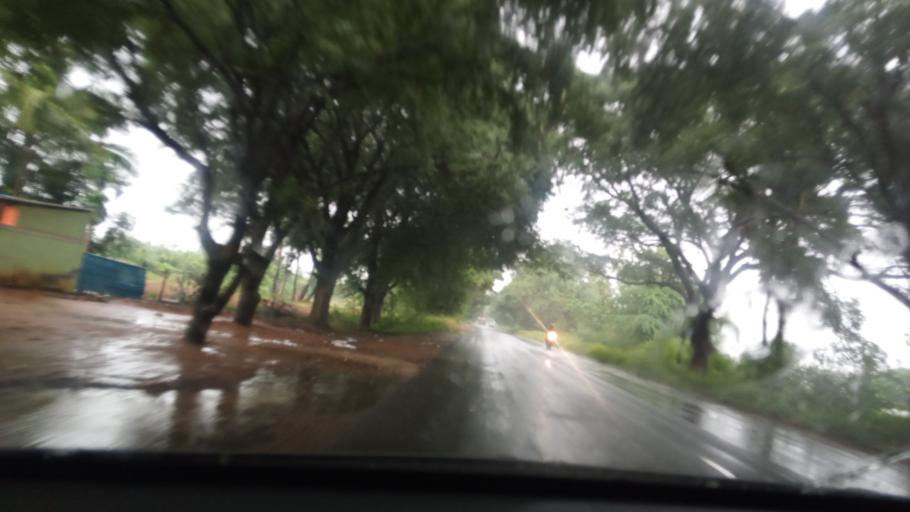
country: IN
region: Tamil Nadu
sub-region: Vellore
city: Kalavai
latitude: 12.8090
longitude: 79.4135
